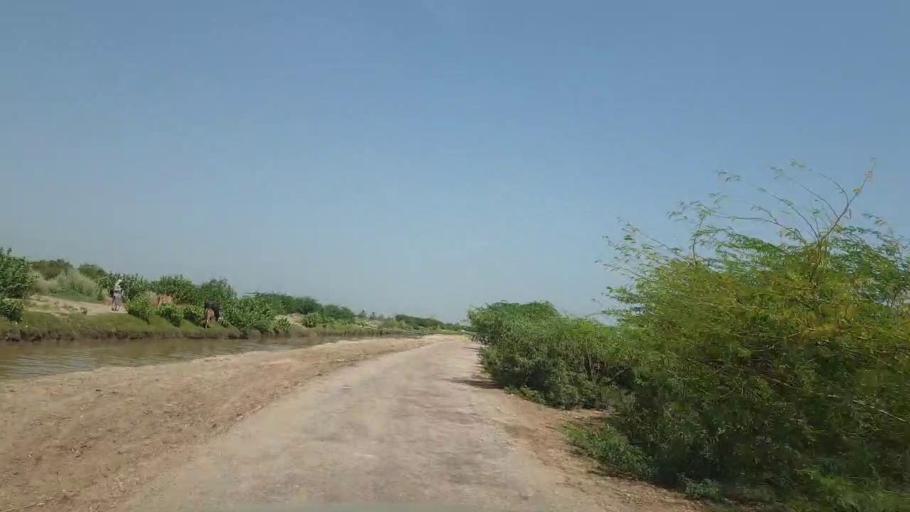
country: PK
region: Sindh
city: Rohri
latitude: 27.6223
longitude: 69.0979
